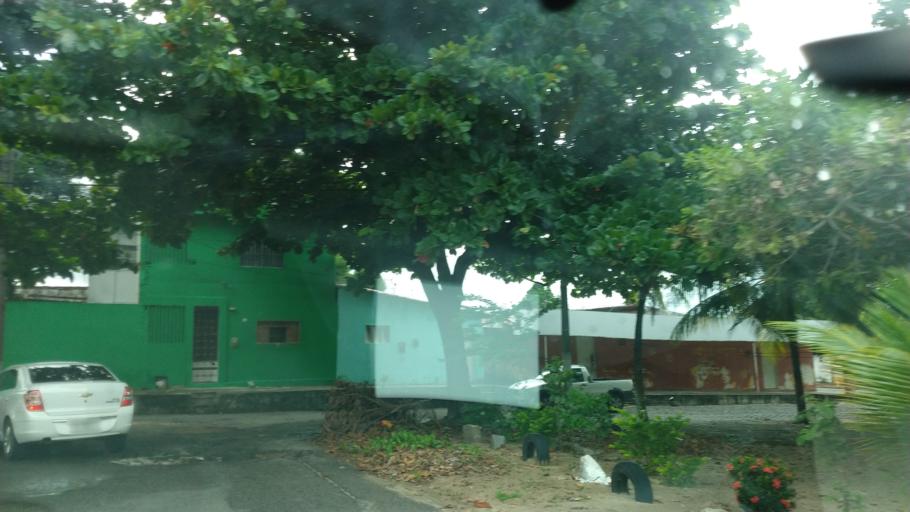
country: BR
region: Rio Grande do Norte
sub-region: Natal
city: Natal
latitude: -5.8629
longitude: -35.2089
